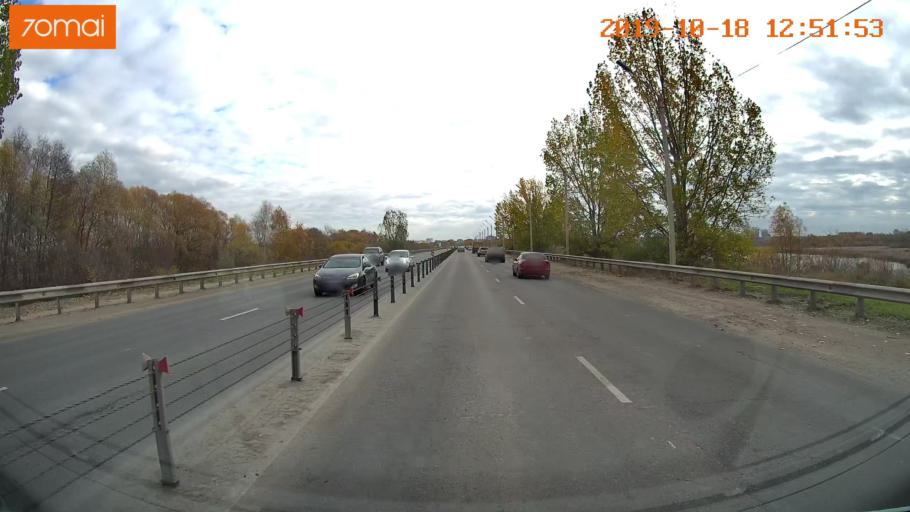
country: RU
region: Rjazan
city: Ryazan'
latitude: 54.6569
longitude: 39.6869
